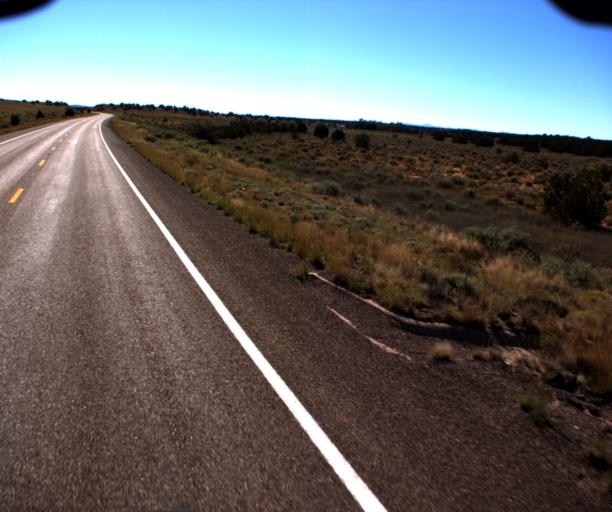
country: US
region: Arizona
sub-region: Apache County
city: Saint Johns
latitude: 34.6111
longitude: -109.6504
